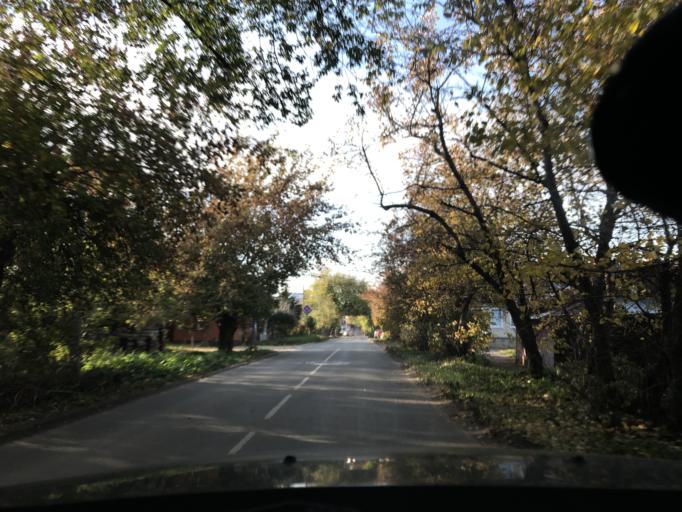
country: RU
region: Tula
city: Tula
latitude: 54.1899
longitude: 37.6315
